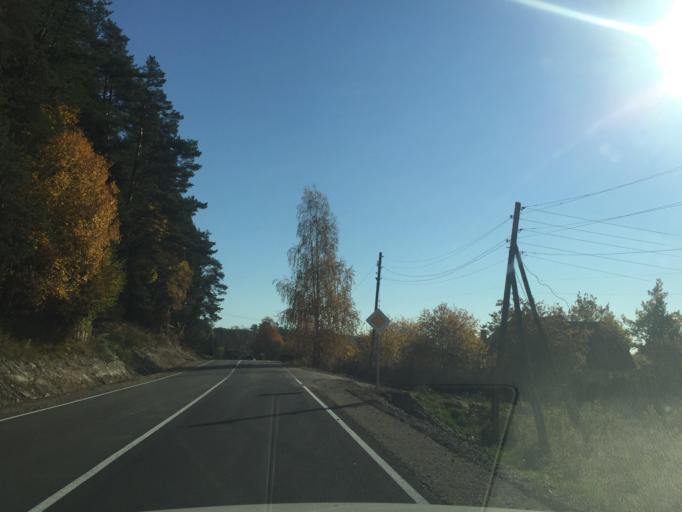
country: RU
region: Leningrad
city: Kuznechnoye
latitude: 61.3029
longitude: 29.8835
